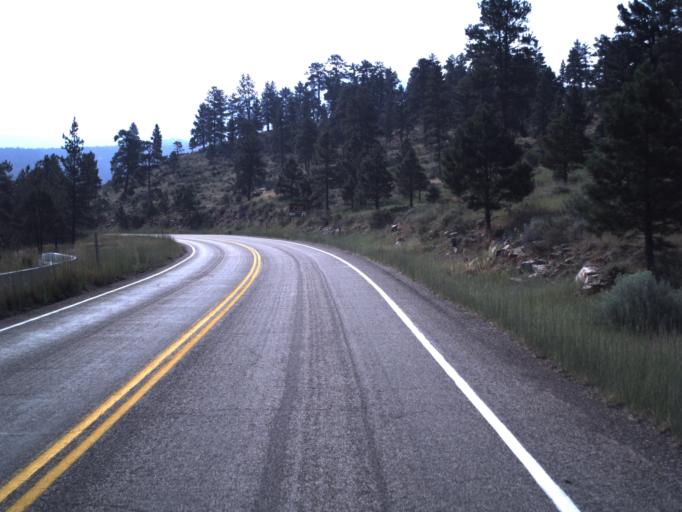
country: US
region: Utah
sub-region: Daggett County
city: Manila
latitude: 40.8968
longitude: -109.4526
